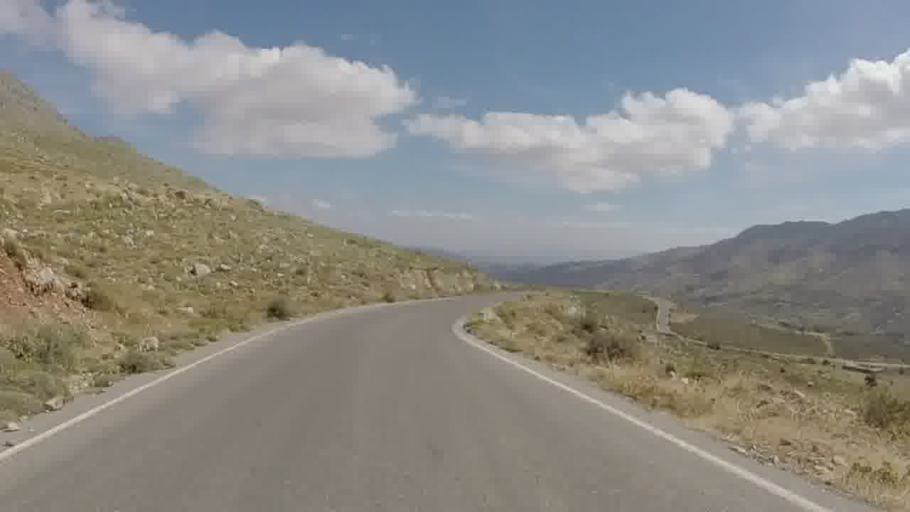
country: GR
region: Crete
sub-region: Nomos Rethymnis
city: Agia Galini
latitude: 35.1555
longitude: 24.6188
